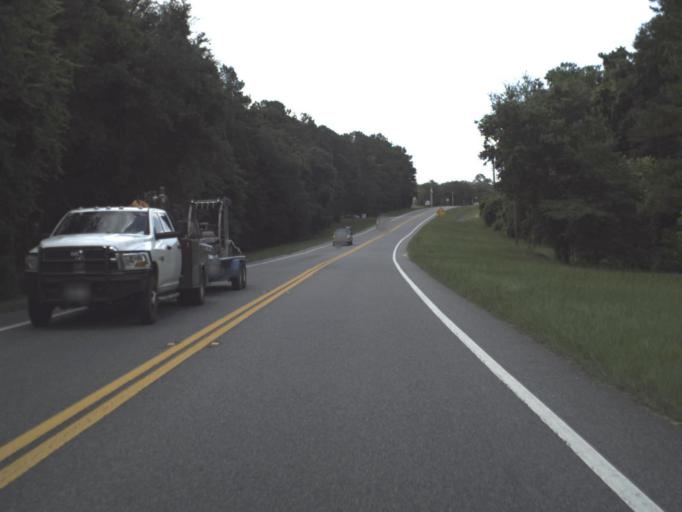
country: US
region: Florida
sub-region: Clay County
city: Asbury Lake
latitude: 29.9811
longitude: -81.8480
